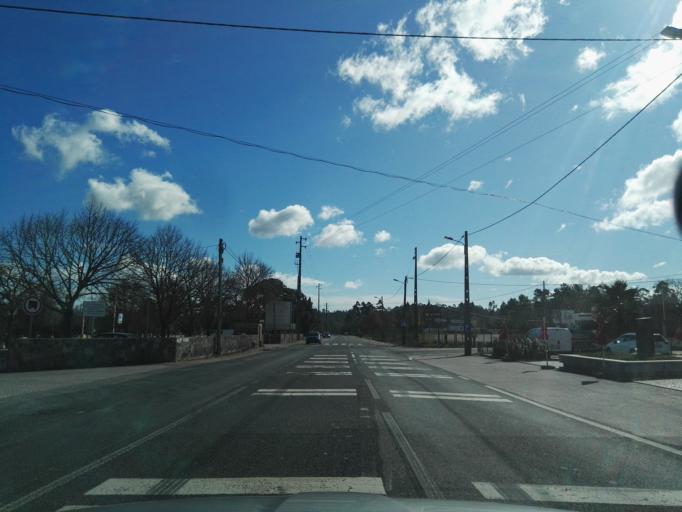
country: PT
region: Santarem
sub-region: Ourem
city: Fatima
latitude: 39.6278
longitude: -8.6801
